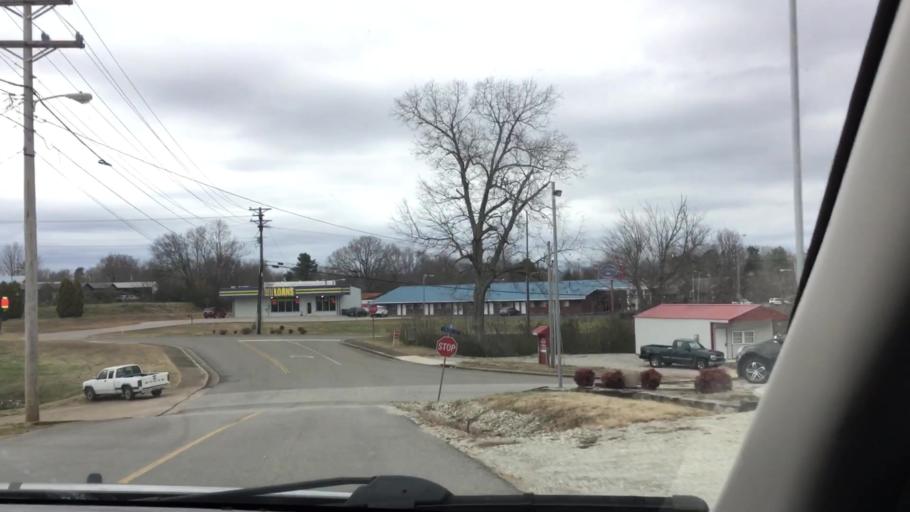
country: US
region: Tennessee
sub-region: Lewis County
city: Hohenwald
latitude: 35.5469
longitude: -87.5494
